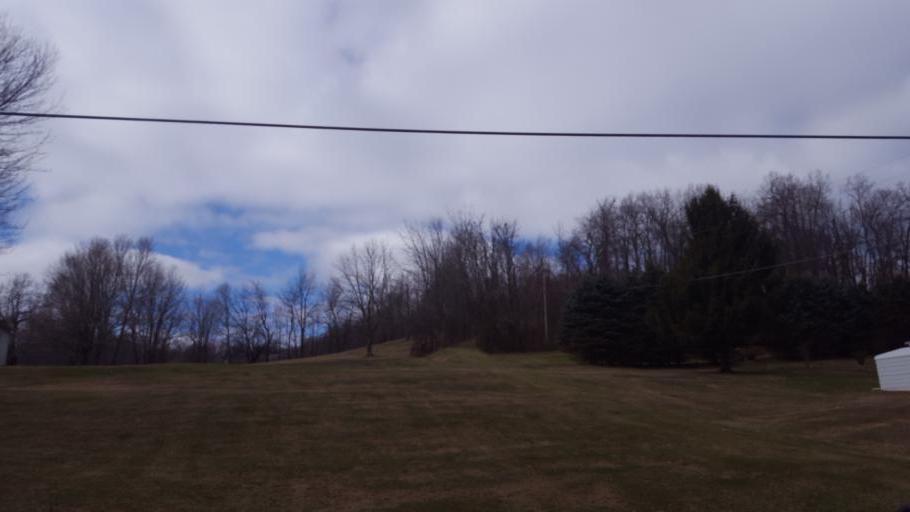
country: US
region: Ohio
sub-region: Sandusky County
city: Bellville
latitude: 40.6734
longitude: -82.5114
